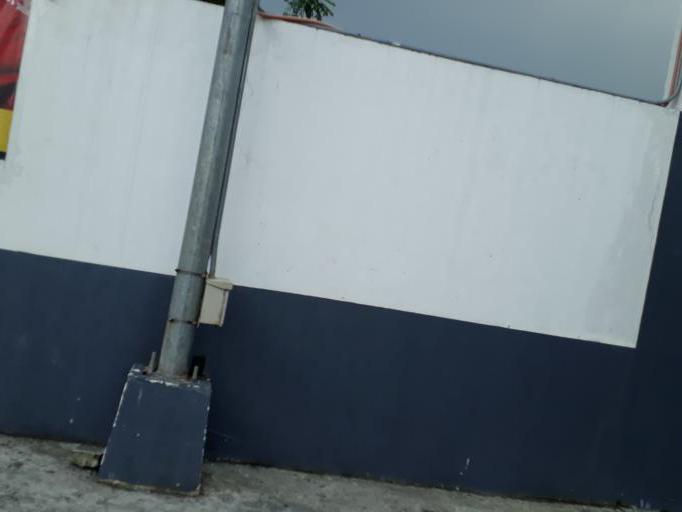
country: PH
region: Calabarzon
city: Bagong Pagasa
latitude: 14.6736
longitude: 121.0525
